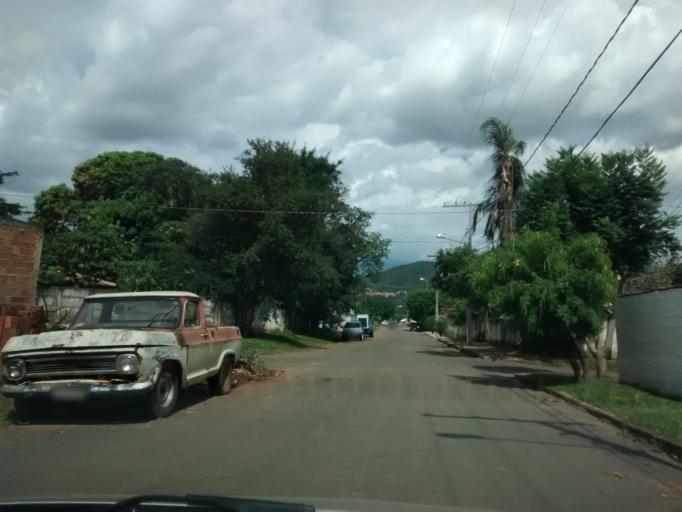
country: BR
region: Goias
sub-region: Pirenopolis
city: Pirenopolis
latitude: -15.8433
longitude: -48.9631
